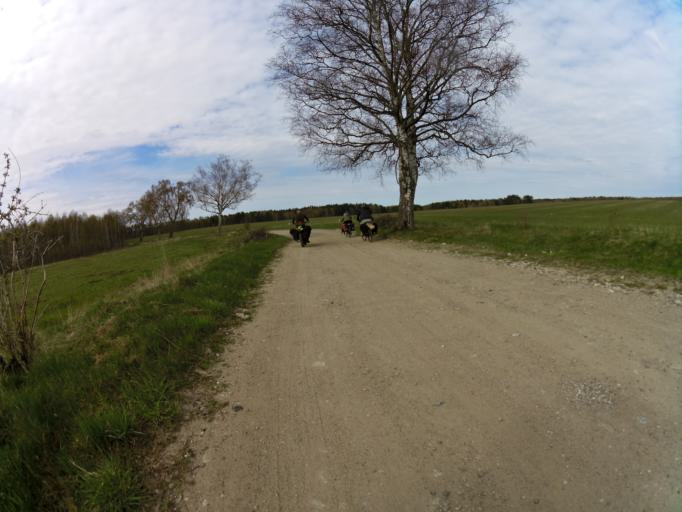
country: PL
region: West Pomeranian Voivodeship
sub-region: Powiat koszalinski
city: Bobolice
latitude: 53.8531
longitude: 16.6866
